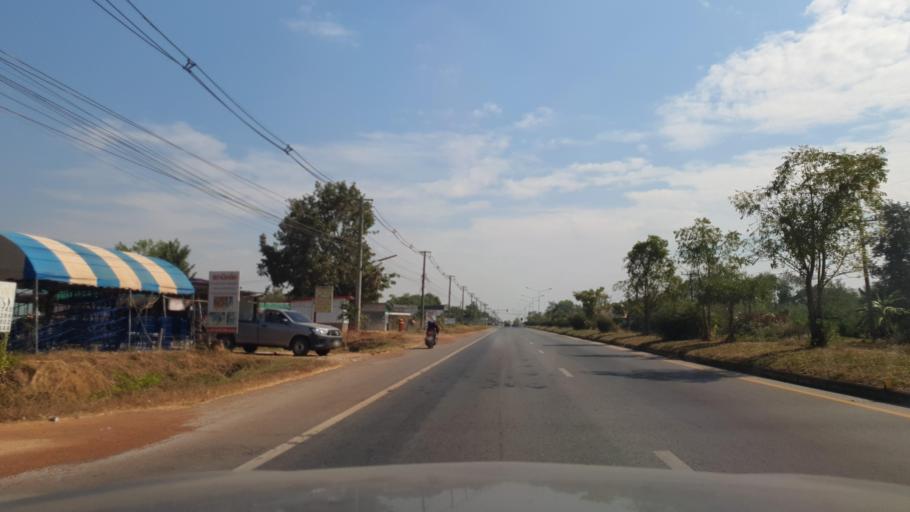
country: TH
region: Maha Sarakham
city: Kantharawichai
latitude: 16.3937
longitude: 103.2954
